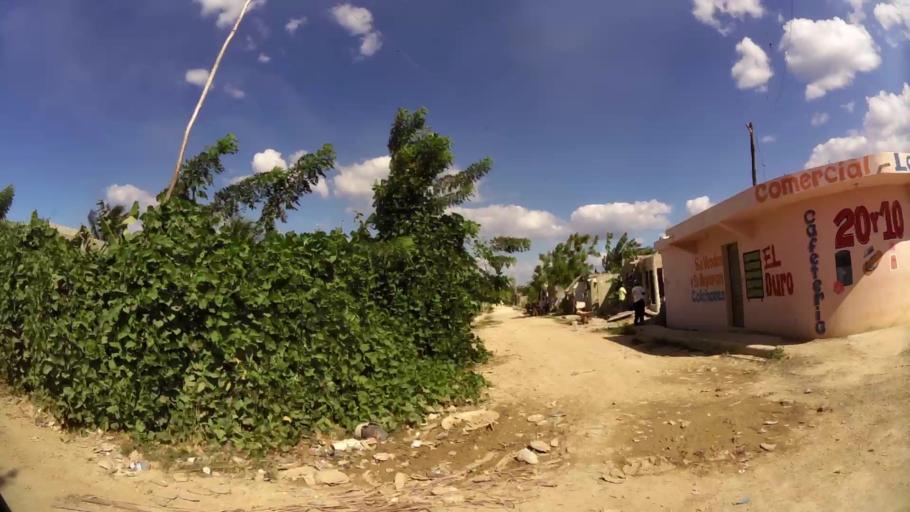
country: DO
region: Santo Domingo
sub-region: Santo Domingo
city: Santo Domingo Este
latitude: 18.4724
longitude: -69.7667
